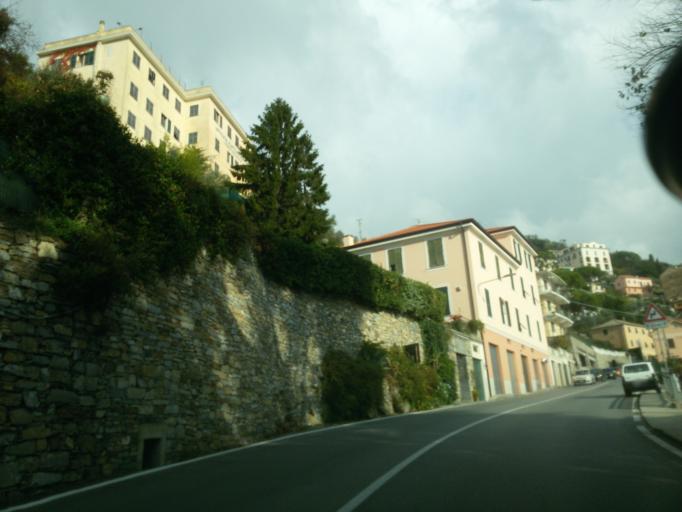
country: IT
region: Liguria
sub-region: Provincia di Genova
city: Camogli
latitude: 44.3477
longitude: 9.1670
